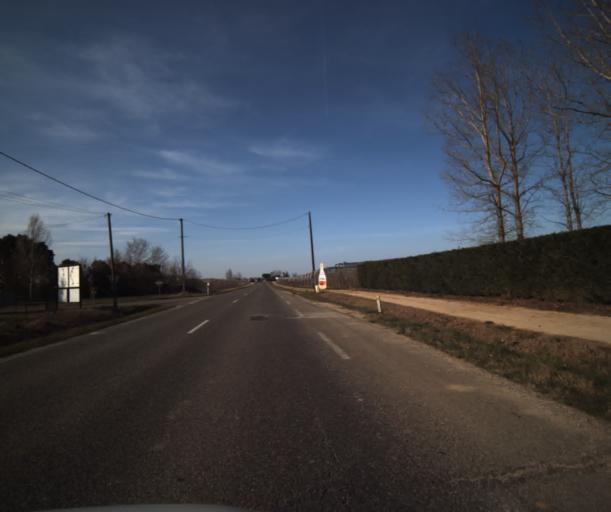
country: FR
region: Midi-Pyrenees
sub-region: Departement du Tarn-et-Garonne
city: Corbarieu
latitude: 43.9383
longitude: 1.3578
